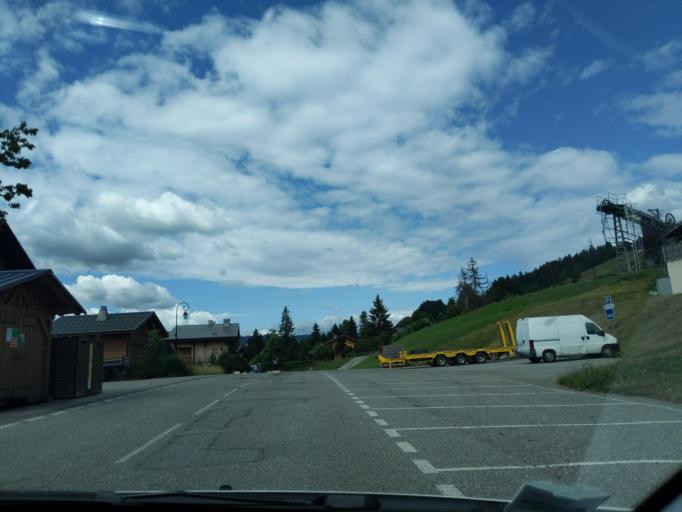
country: FR
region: Rhone-Alpes
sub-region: Departement de la Haute-Savoie
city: Praz-sur-Arly
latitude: 45.7847
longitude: 6.5004
